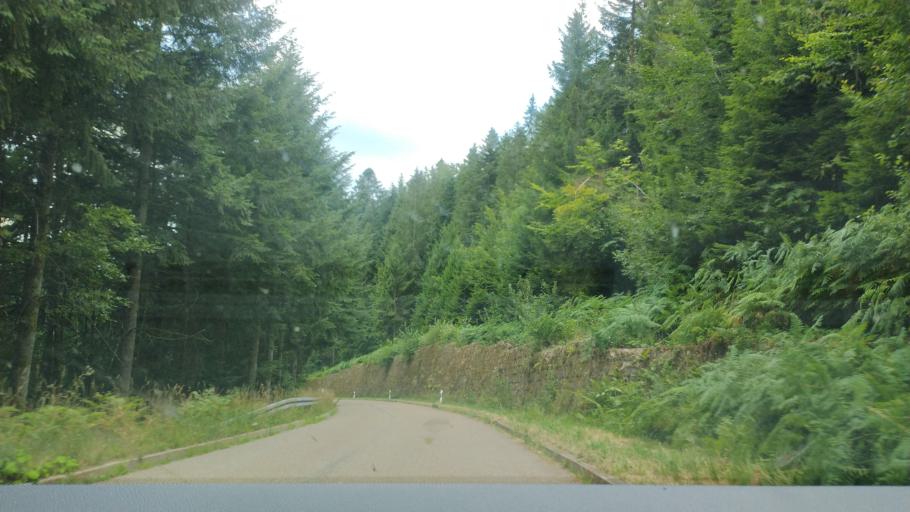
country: DE
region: Baden-Wuerttemberg
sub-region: Freiburg Region
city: Oppenau
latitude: 48.4342
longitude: 8.1514
